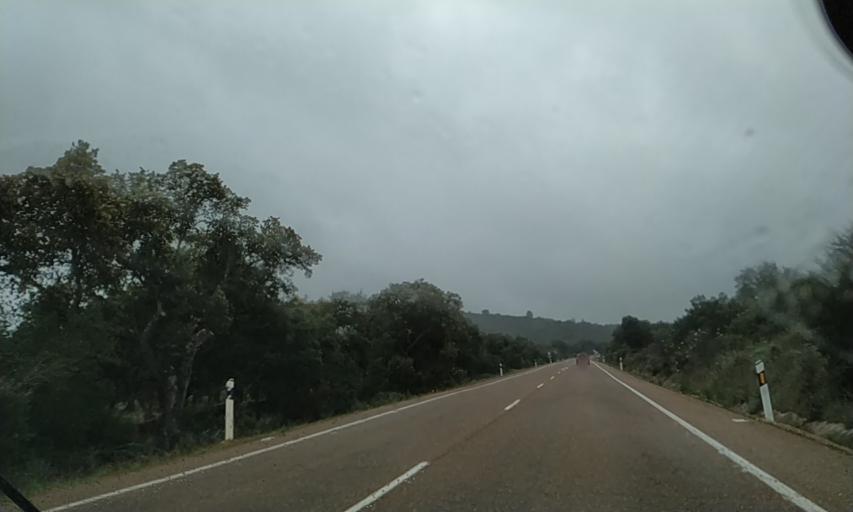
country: ES
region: Extremadura
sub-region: Provincia de Badajoz
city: Puebla de Obando
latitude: 39.1927
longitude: -6.5958
